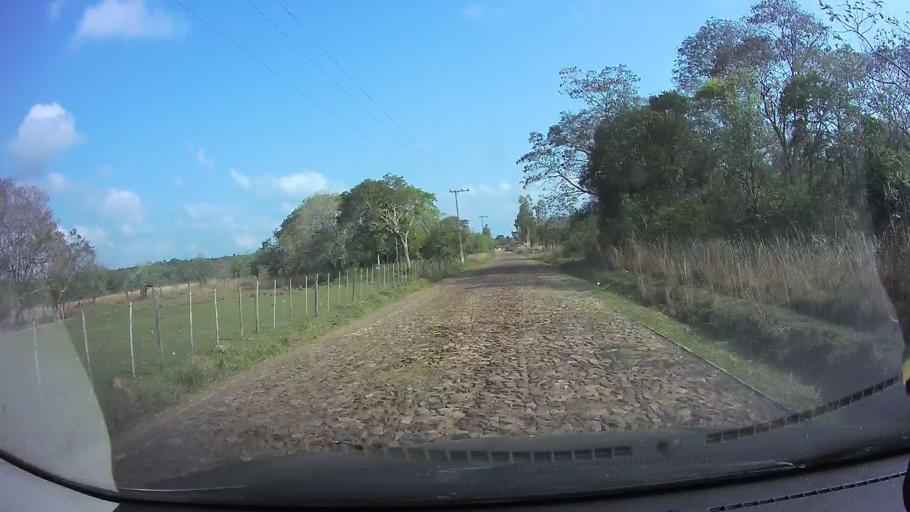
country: PY
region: Cordillera
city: Arroyos y Esteros
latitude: -24.9931
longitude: -57.1929
